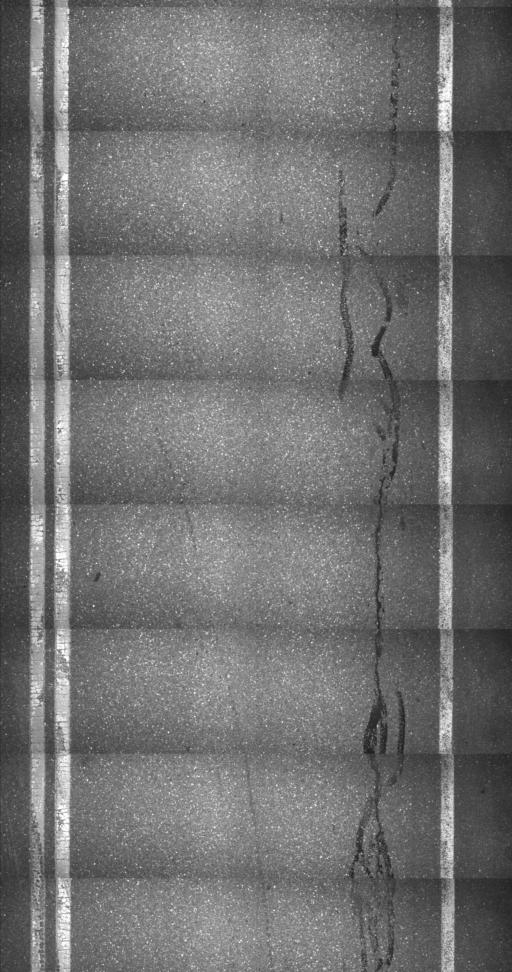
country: US
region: Vermont
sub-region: Windham County
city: Brattleboro
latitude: 42.8166
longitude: -72.5476
